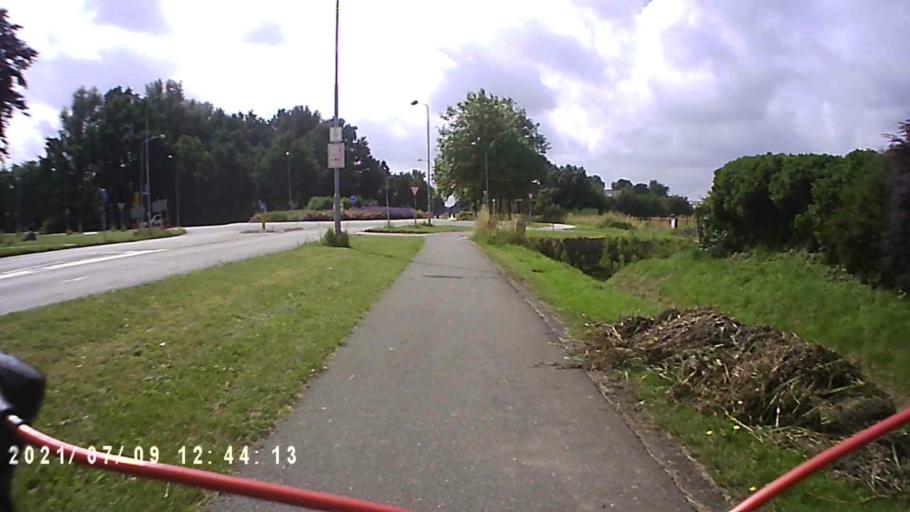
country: NL
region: Groningen
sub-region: Gemeente  Oldambt
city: Winschoten
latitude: 53.1334
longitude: 7.0228
